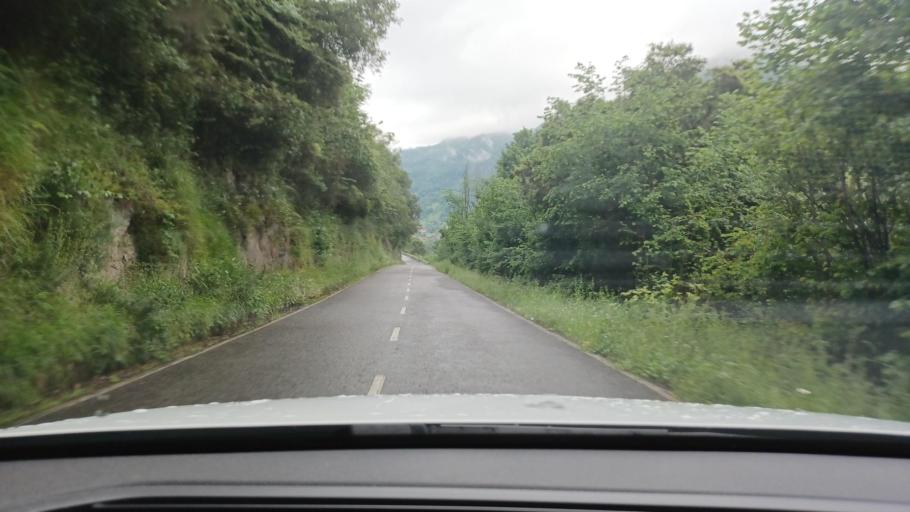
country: ES
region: Asturias
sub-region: Province of Asturias
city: Proaza
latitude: 43.2850
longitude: -5.9818
